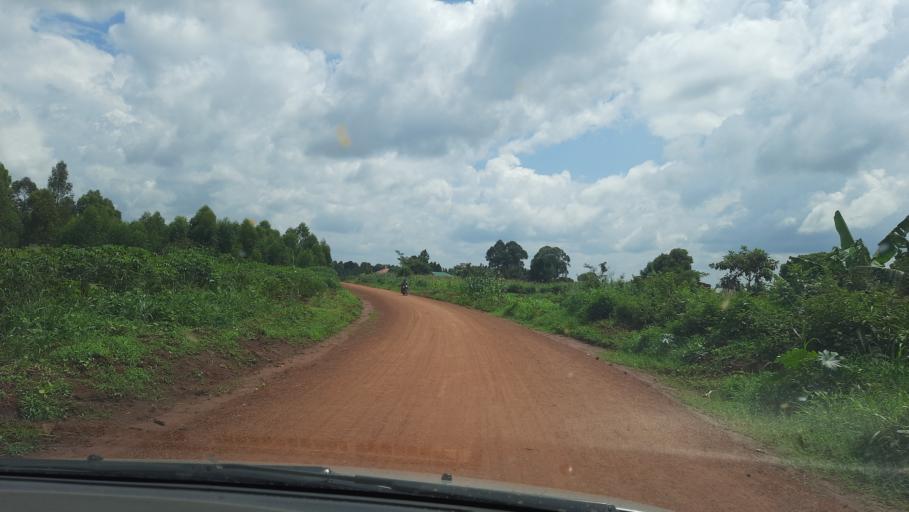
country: UG
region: Western Region
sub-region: Kiryandongo District
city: Kiryandongo
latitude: 1.8194
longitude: 31.9853
